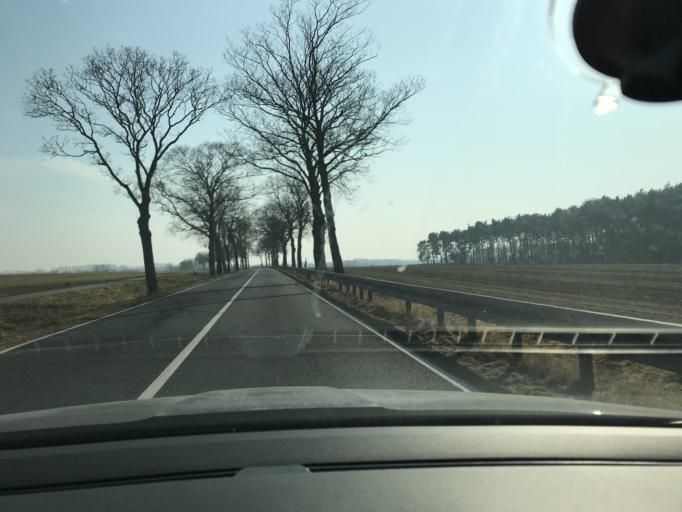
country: DE
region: Brandenburg
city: Mittenwalde
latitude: 52.2883
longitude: 13.5237
